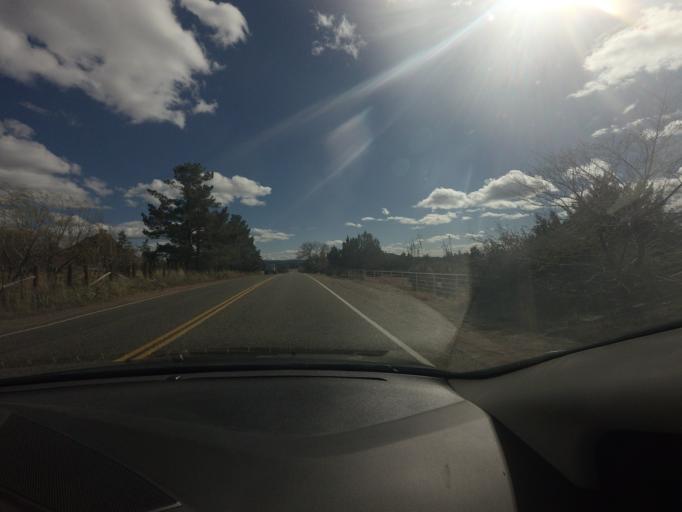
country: US
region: Arizona
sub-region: Yavapai County
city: West Sedona
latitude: 34.8795
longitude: -111.8211
